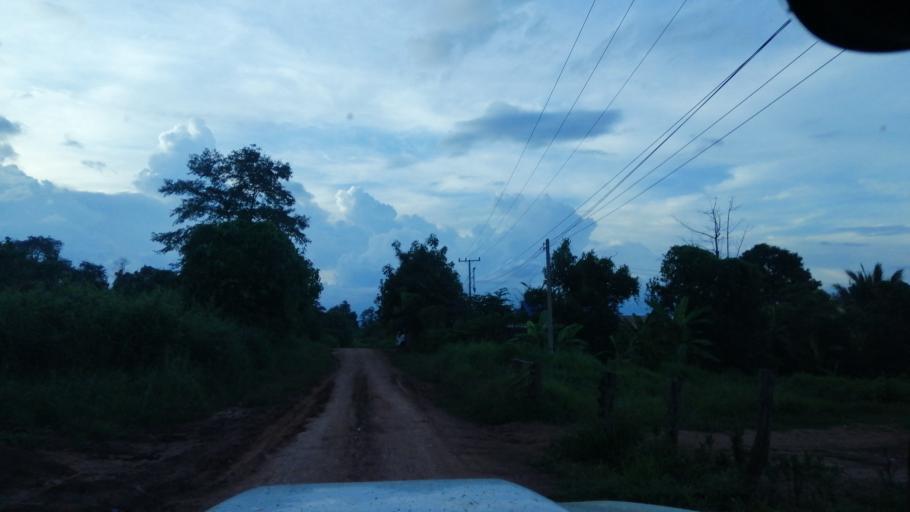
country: TH
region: Uttaradit
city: Ban Khok
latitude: 17.8708
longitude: 101.0871
